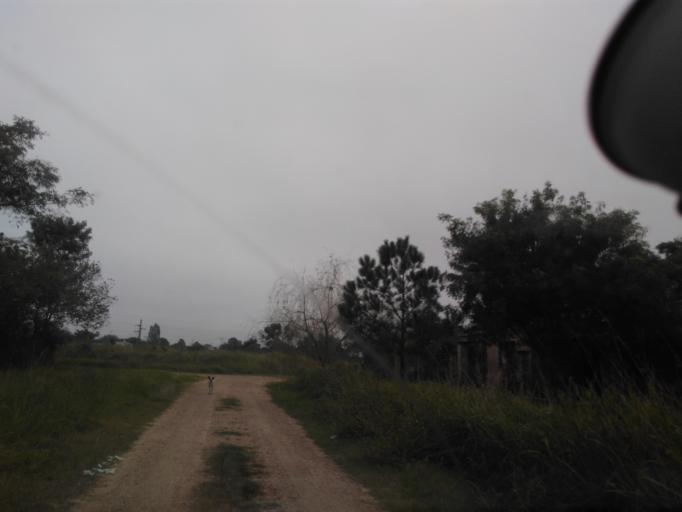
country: AR
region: Chaco
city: Fontana
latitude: -27.4024
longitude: -58.9956
